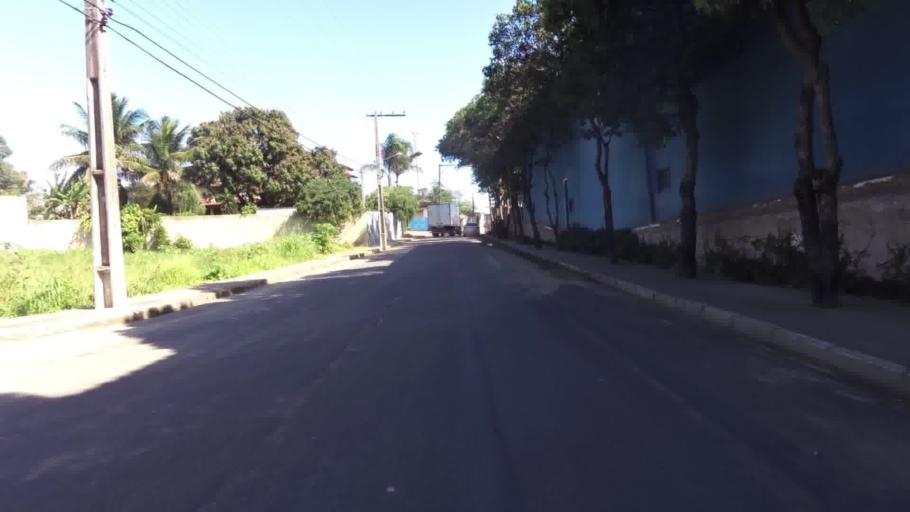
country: BR
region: Espirito Santo
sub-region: Piuma
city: Piuma
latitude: -20.8184
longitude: -40.6265
